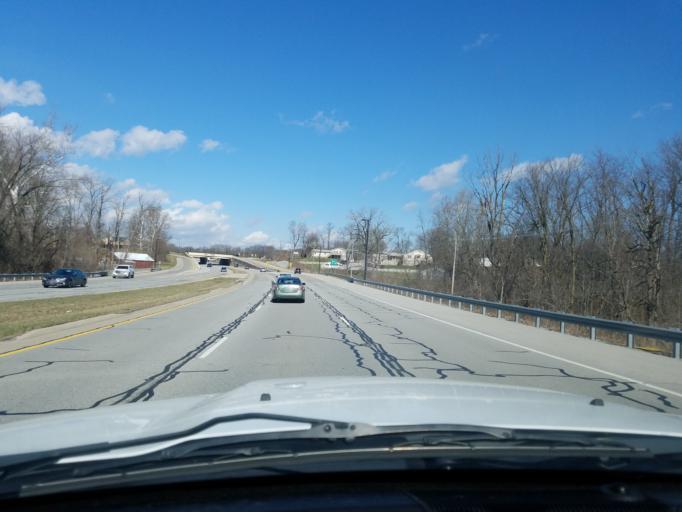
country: US
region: Indiana
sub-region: Hamilton County
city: Carmel
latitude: 39.9826
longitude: -86.1129
